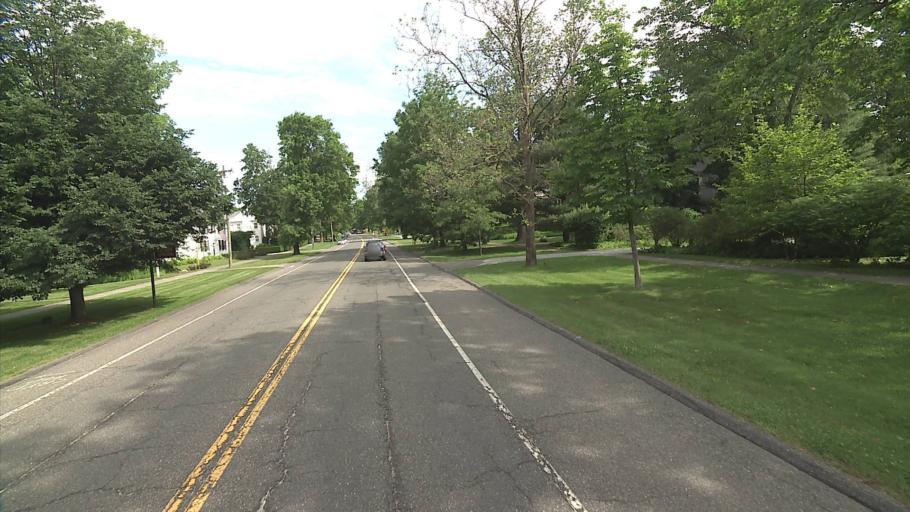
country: US
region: Connecticut
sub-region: Litchfield County
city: Litchfield
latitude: 41.7438
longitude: -73.1880
